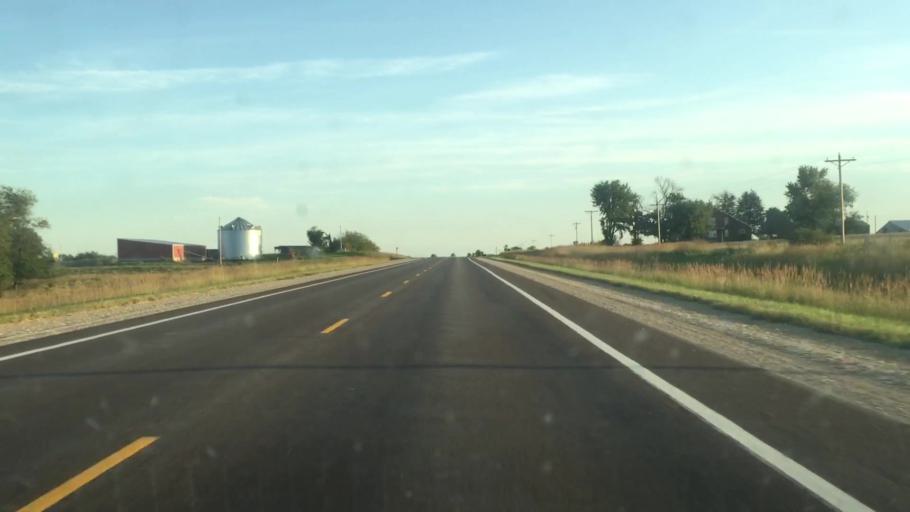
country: US
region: Kansas
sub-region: Atchison County
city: Atchison
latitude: 39.4431
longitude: -95.0933
